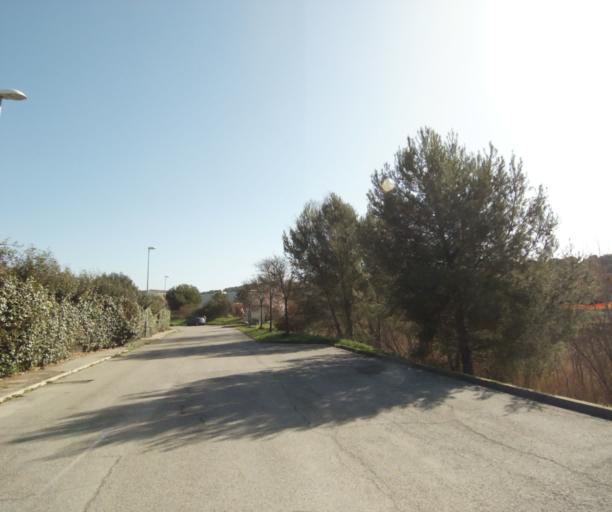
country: FR
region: Provence-Alpes-Cote d'Azur
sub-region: Departement des Bouches-du-Rhone
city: Cabries
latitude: 43.4249
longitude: 5.3889
